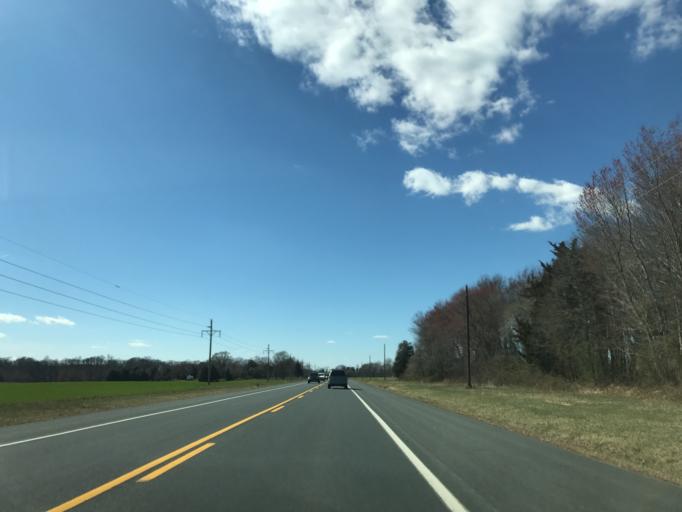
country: US
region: Maryland
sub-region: Queen Anne's County
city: Kingstown
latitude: 39.2563
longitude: -75.9741
